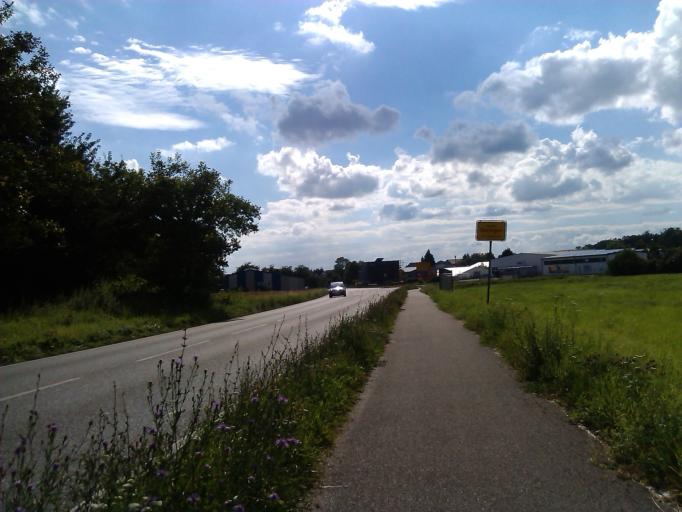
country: DE
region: Baden-Wuerttemberg
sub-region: Karlsruhe Region
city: Ostringen
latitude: 49.2257
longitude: 8.7297
